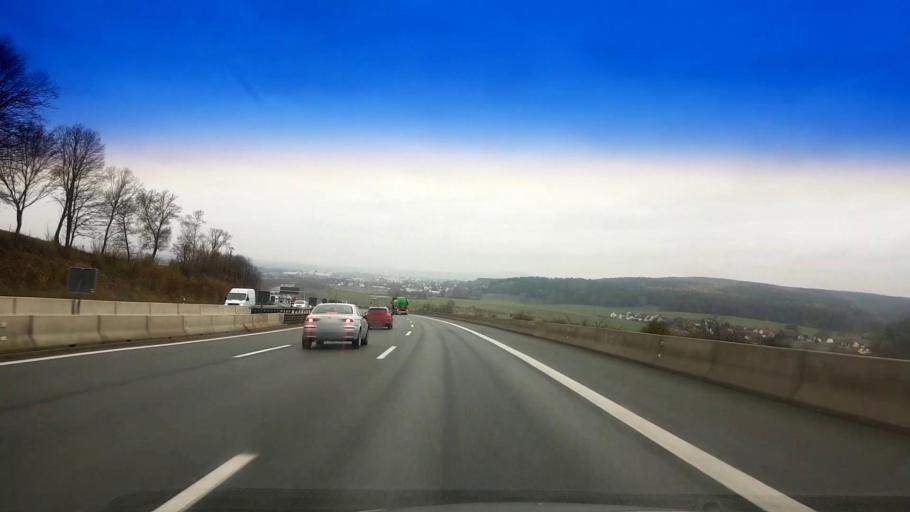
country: DE
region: Bavaria
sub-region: Upper Franconia
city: Bindlach
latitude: 49.9995
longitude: 11.6075
